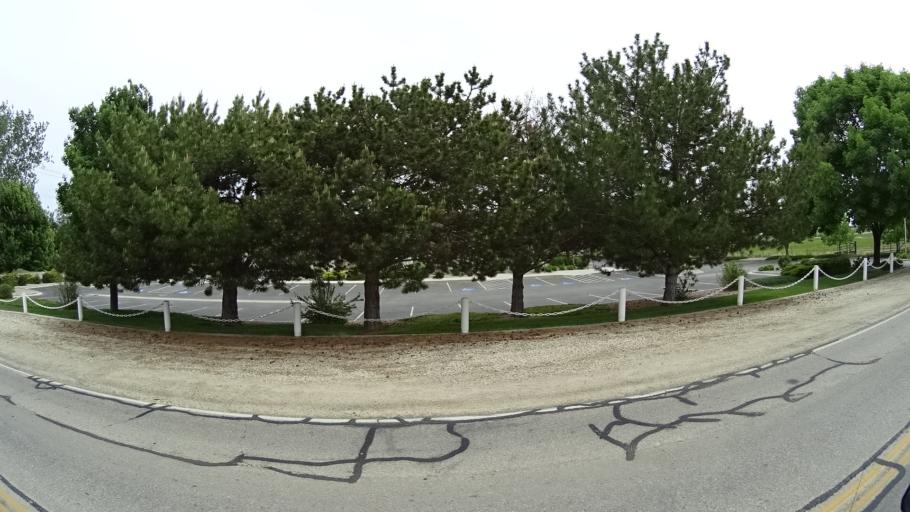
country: US
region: Idaho
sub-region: Ada County
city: Meridian
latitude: 43.5608
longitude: -116.3745
